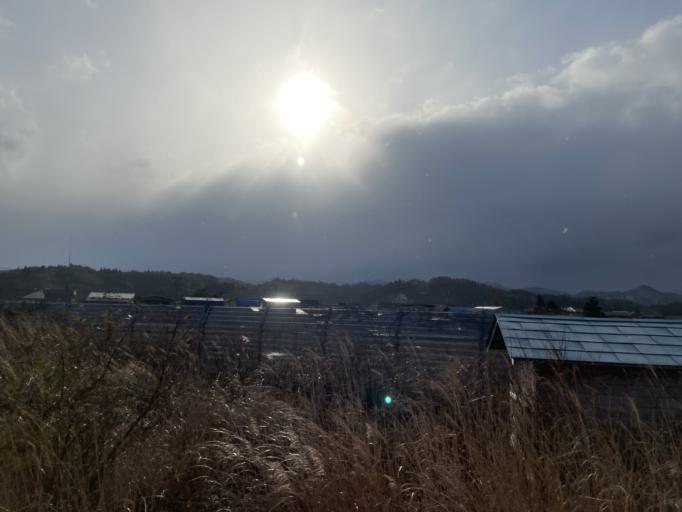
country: JP
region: Aomori
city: Aomori Shi
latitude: 41.0517
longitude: 140.5965
